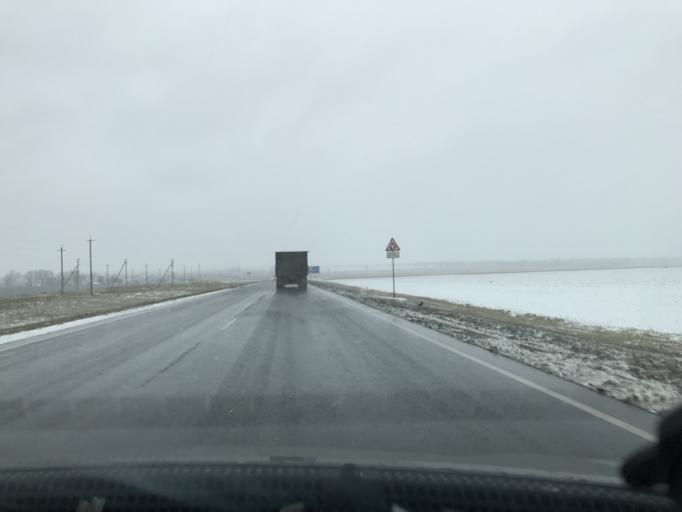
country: RU
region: Rostov
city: Yegorlykskaya
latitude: 46.5721
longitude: 40.6310
